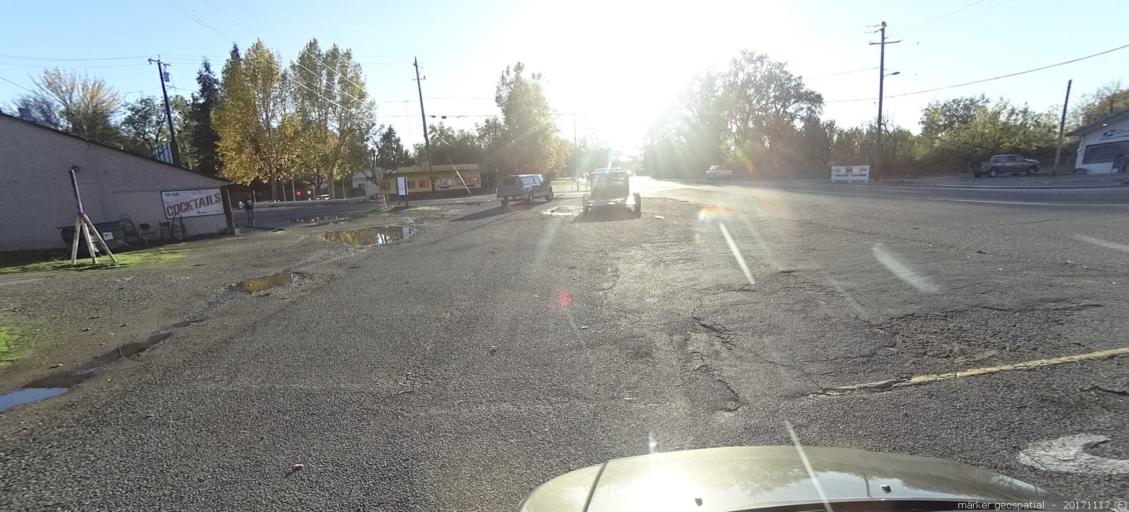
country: US
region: California
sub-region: Shasta County
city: Anderson
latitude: 40.4486
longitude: -122.2564
